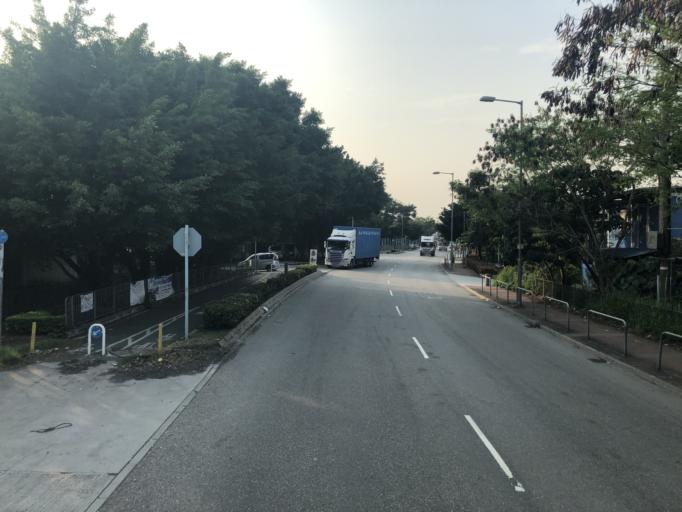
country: HK
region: Yuen Long
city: Yuen Long Kau Hui
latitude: 22.4582
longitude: 113.9909
